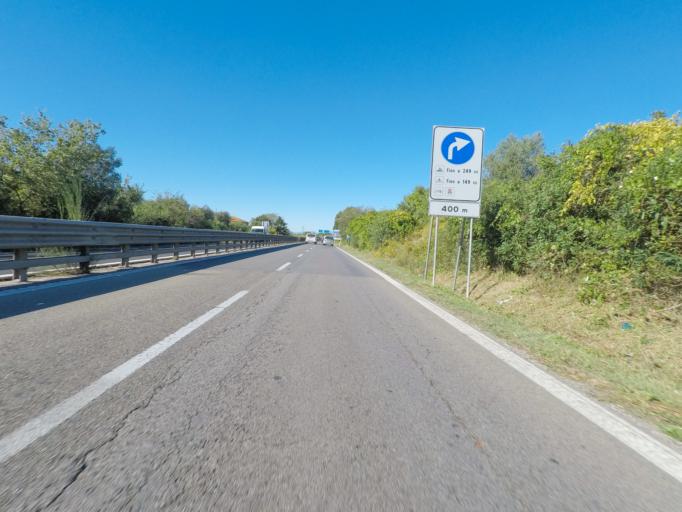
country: IT
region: Tuscany
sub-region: Provincia di Grosseto
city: Grosseto
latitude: 42.7246
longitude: 11.1375
